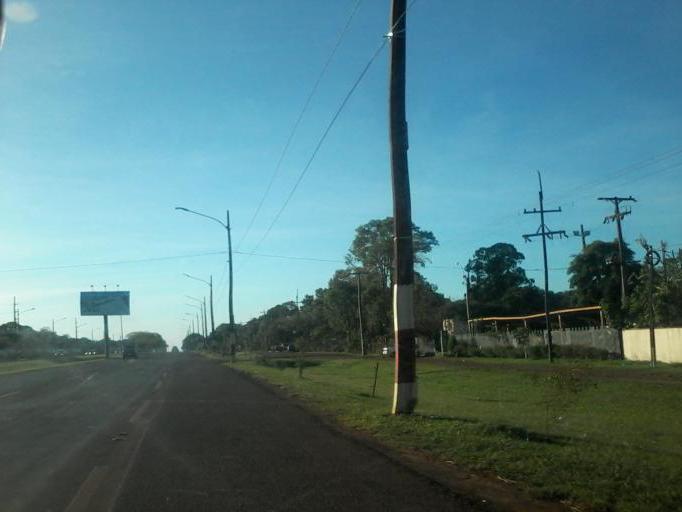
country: PY
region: Alto Parana
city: Ciudad del Este
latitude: -25.4397
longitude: -54.6344
